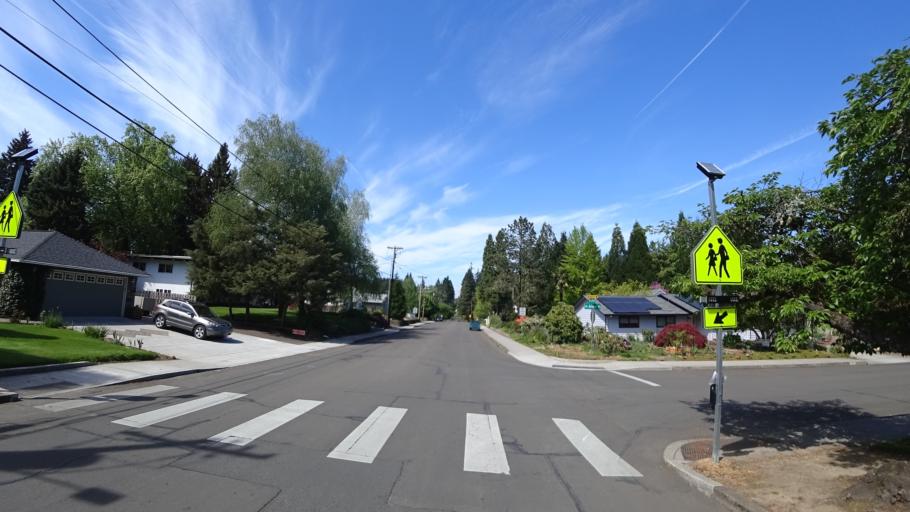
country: US
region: Oregon
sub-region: Washington County
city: Hillsboro
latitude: 45.5133
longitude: -122.9582
